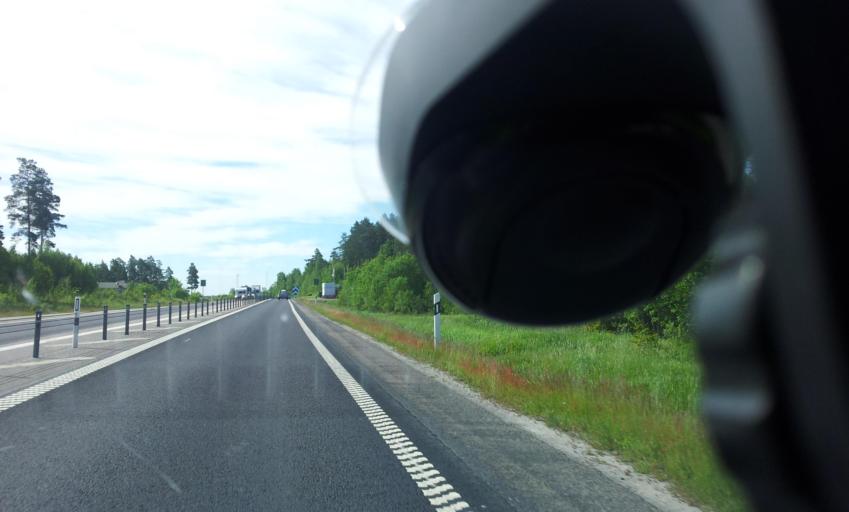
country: SE
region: OEstergoetland
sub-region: Soderkopings Kommun
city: Soederkoeping
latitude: 58.4999
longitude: 16.3016
